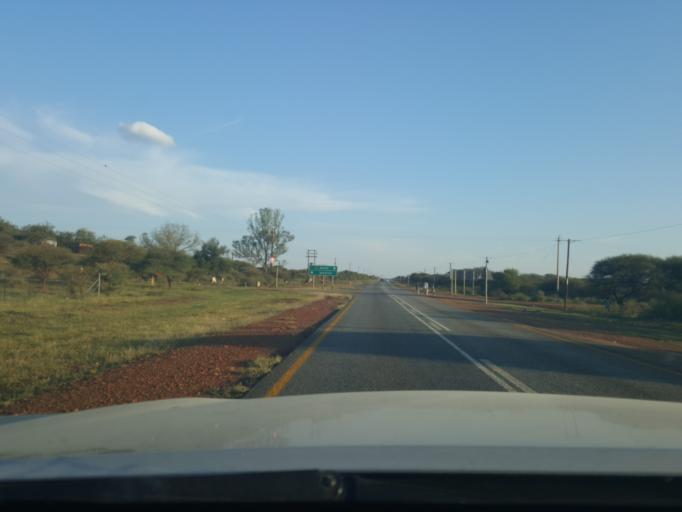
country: ZA
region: North-West
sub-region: Ngaka Modiri Molema District Municipality
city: Zeerust
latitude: -25.4017
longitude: 26.0841
